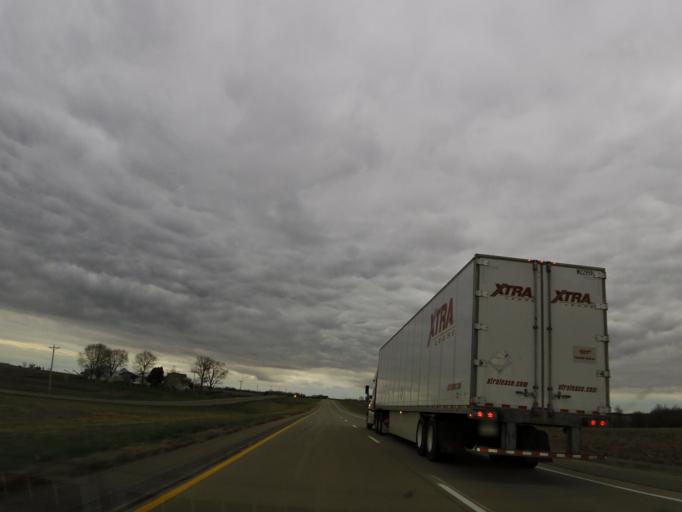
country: US
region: Iowa
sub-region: Henry County
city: Mount Pleasant
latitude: 41.0538
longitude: -91.5448
